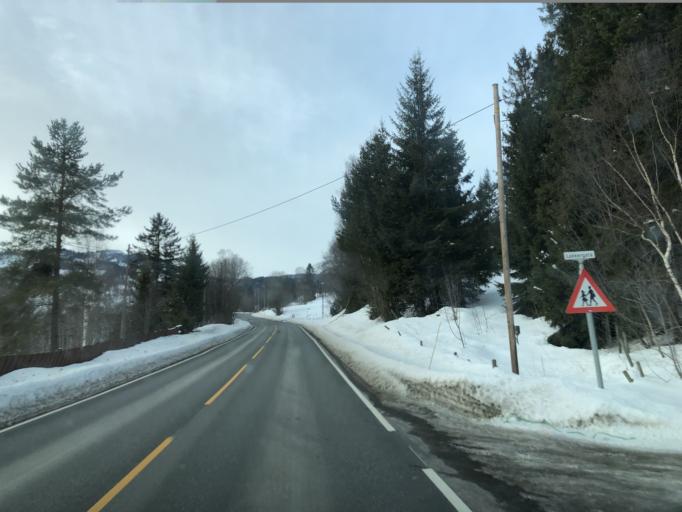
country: NO
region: Oppland
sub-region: Gausdal
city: Segalstad bru
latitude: 61.2655
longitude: 10.1538
